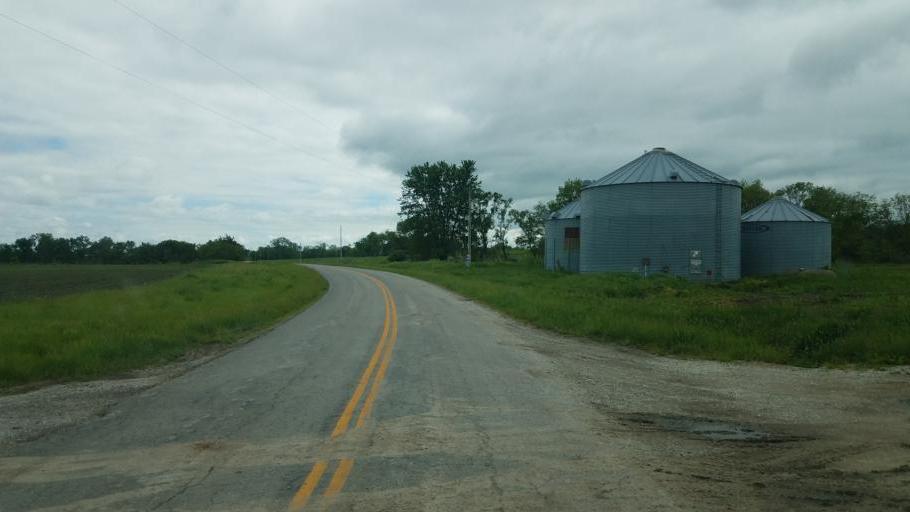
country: US
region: Iowa
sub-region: Decatur County
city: Lamoni
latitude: 40.4791
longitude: -93.8220
